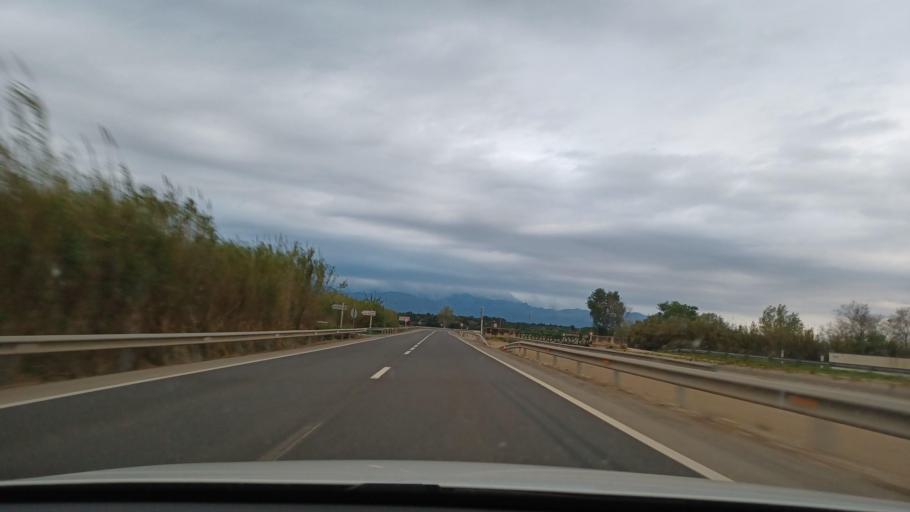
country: ES
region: Catalonia
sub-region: Provincia de Tarragona
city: Masdenverge
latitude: 40.7539
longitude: 0.5419
